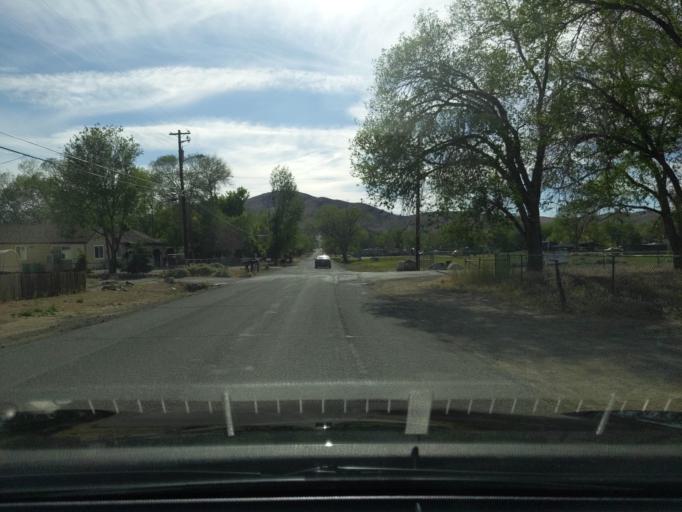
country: US
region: Nevada
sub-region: Washoe County
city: Sun Valley
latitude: 39.5855
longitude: -119.7729
